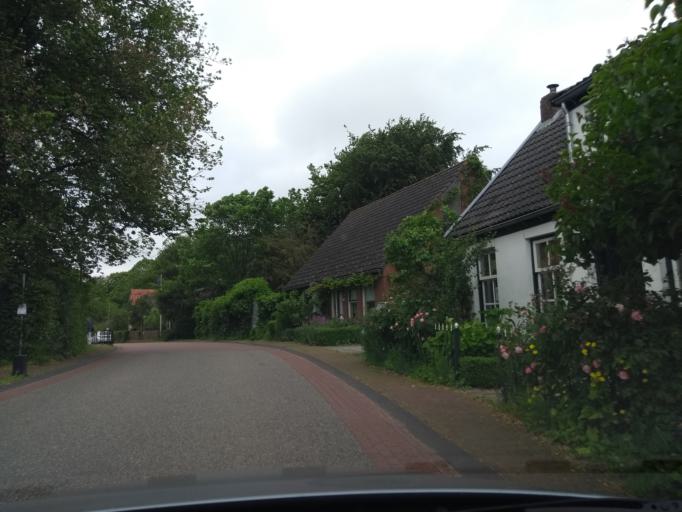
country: NL
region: Groningen
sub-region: Gemeente Zuidhorn
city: Oldehove
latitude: 53.3425
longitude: 6.4254
